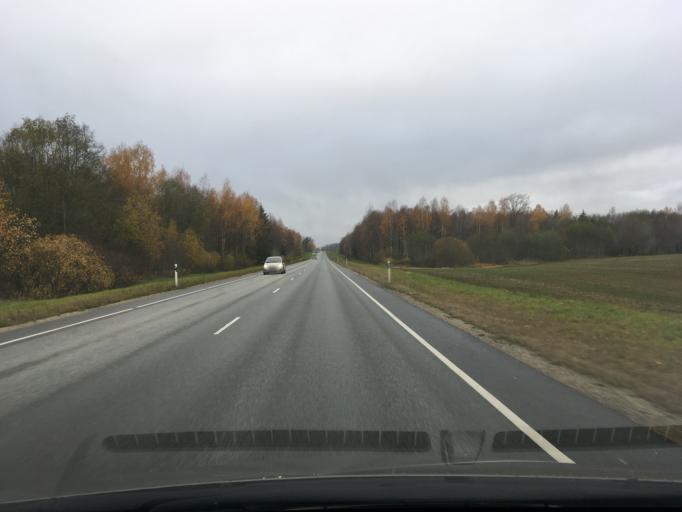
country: EE
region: Tartu
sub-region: Noo vald
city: Noo
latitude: 58.2892
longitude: 26.5595
